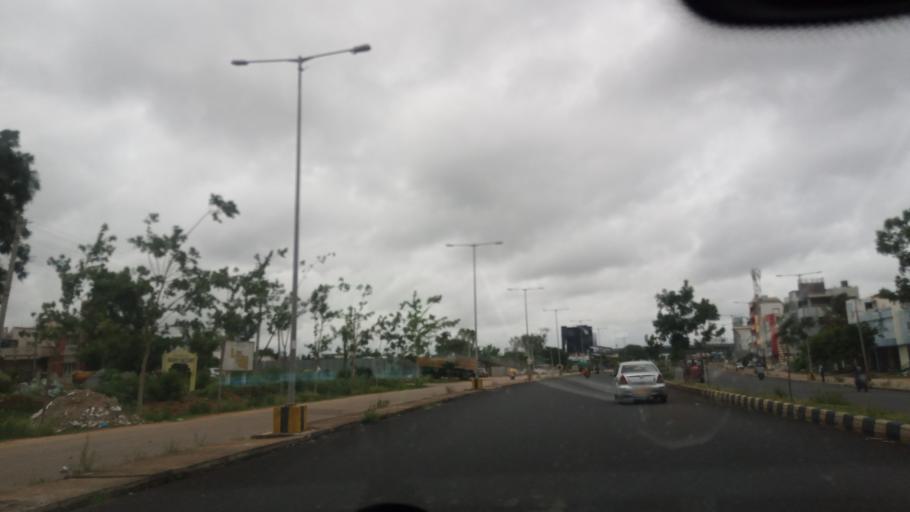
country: IN
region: Karnataka
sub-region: Mysore
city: Mysore
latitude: 12.3296
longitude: 76.5976
